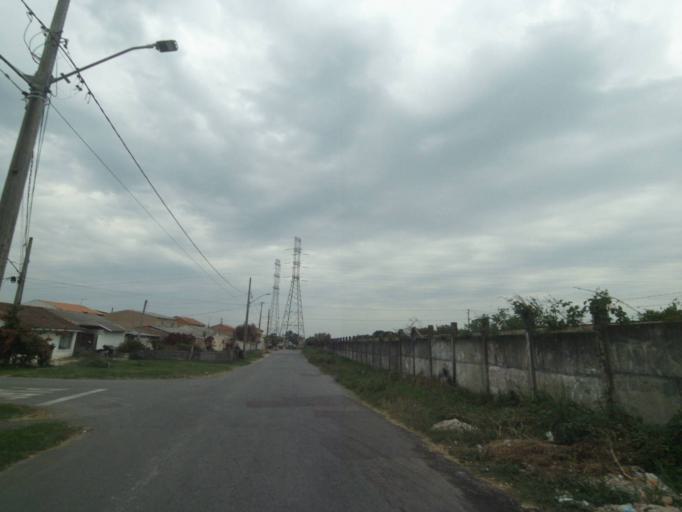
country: BR
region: Parana
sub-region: Pinhais
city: Pinhais
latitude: -25.4835
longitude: -49.1998
